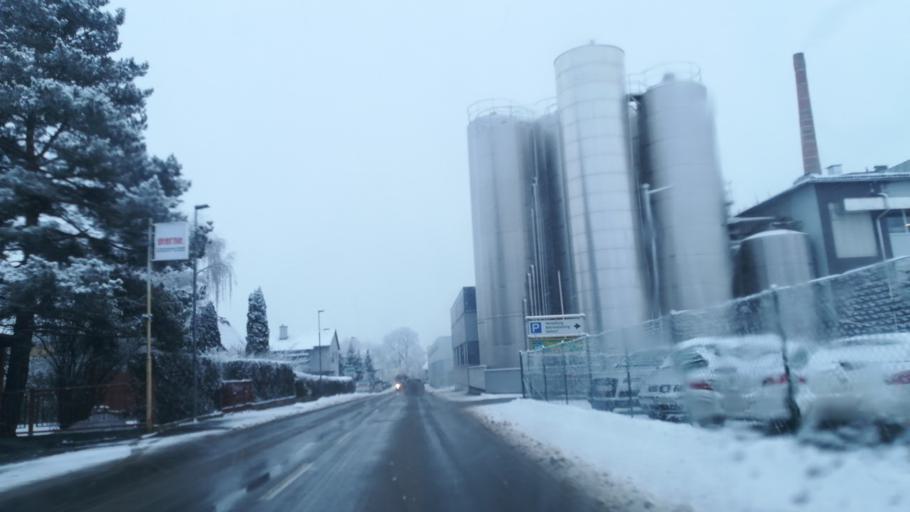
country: AT
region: Styria
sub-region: Politischer Bezirk Murtal
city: Knittelfeld
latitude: 47.2167
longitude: 14.8225
